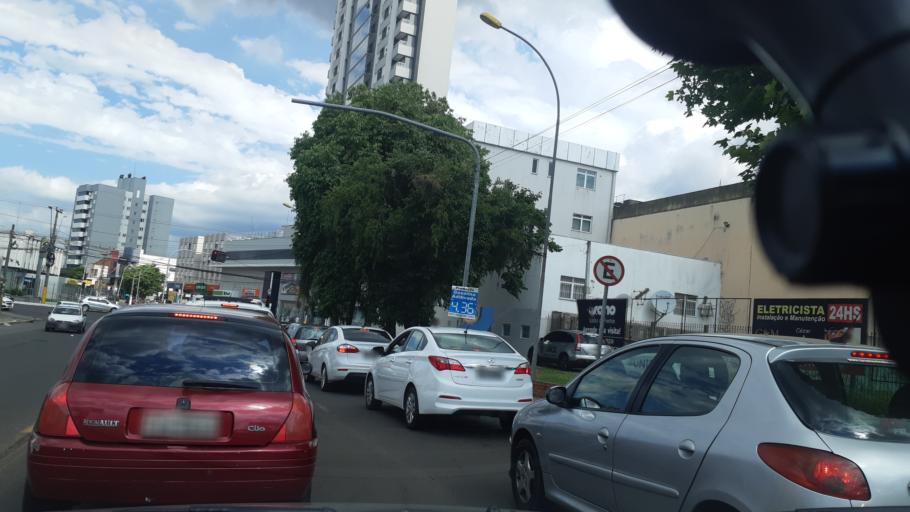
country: BR
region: Rio Grande do Sul
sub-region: Esteio
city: Esteio
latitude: -29.8500
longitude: -51.1776
